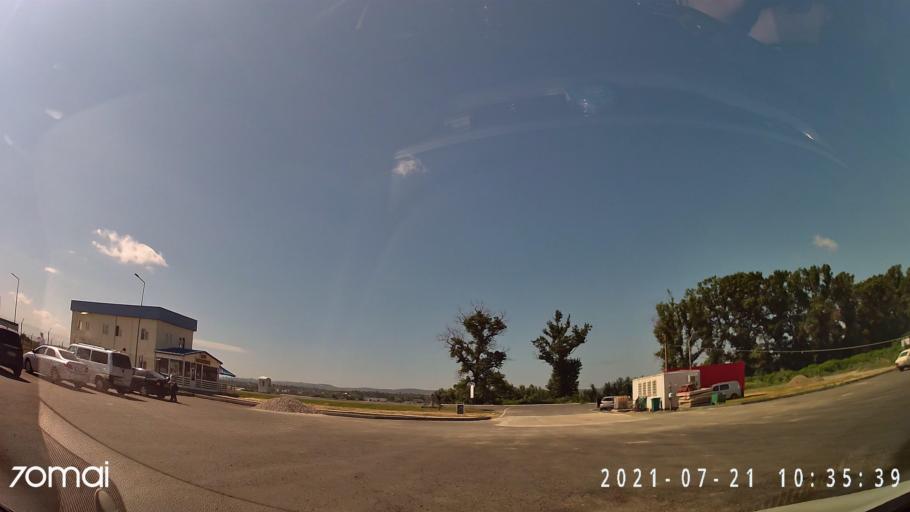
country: RO
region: Tulcea
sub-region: Oras Isaccea
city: Isaccea
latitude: 45.2934
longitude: 28.4567
